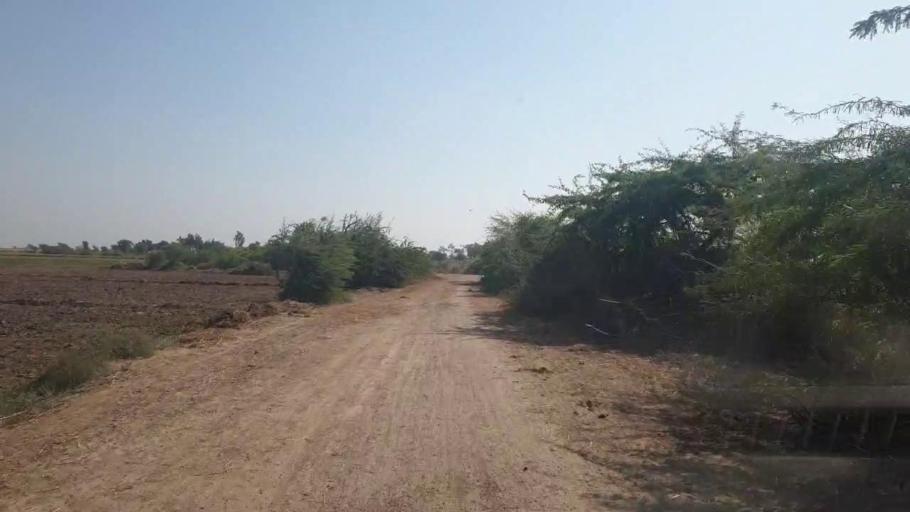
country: PK
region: Sindh
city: Badin
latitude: 24.5456
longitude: 68.8448
